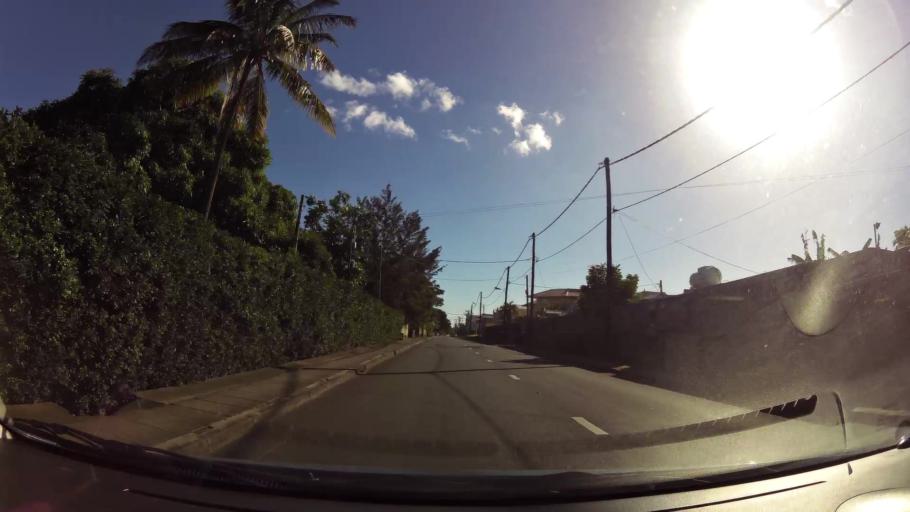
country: MU
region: Black River
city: Grande Riviere Noire
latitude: -20.3475
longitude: 57.3643
